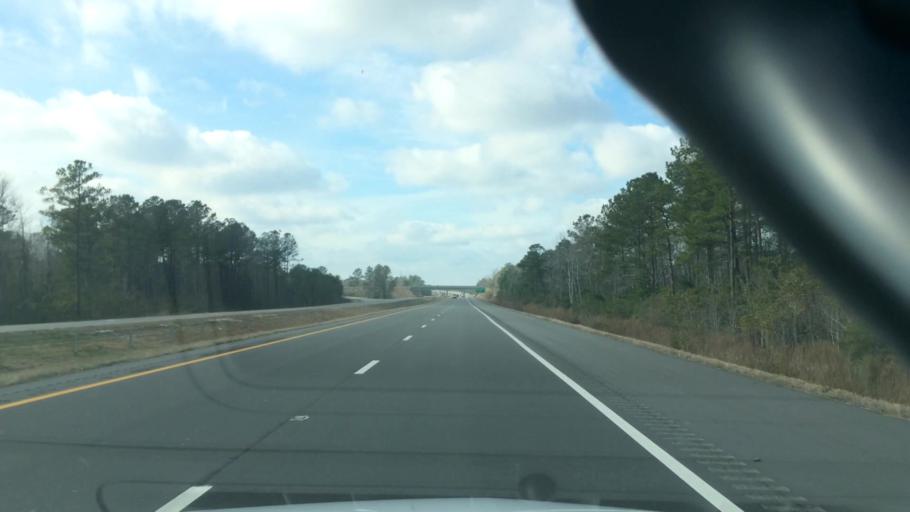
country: US
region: North Carolina
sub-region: Brunswick County
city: Leland
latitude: 34.2761
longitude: -78.0420
